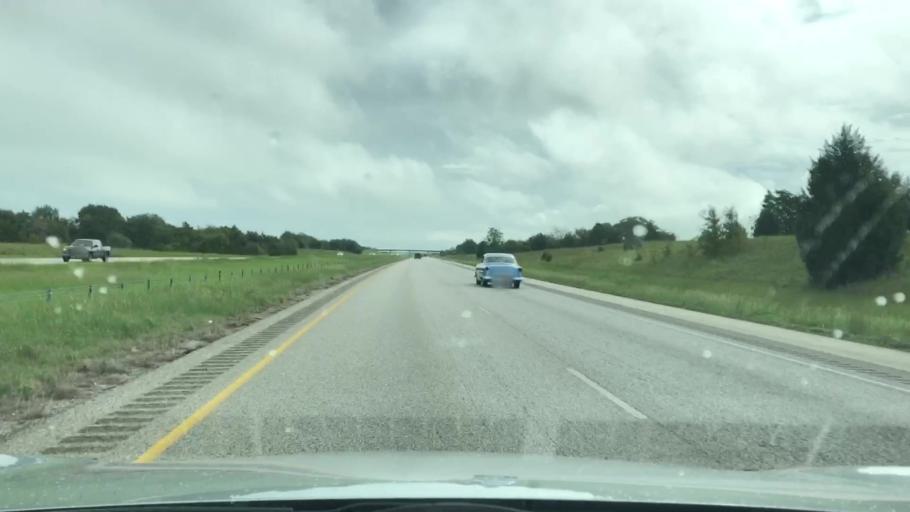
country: US
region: Texas
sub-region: Fayette County
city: Schulenburg
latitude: 29.6910
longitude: -96.9779
